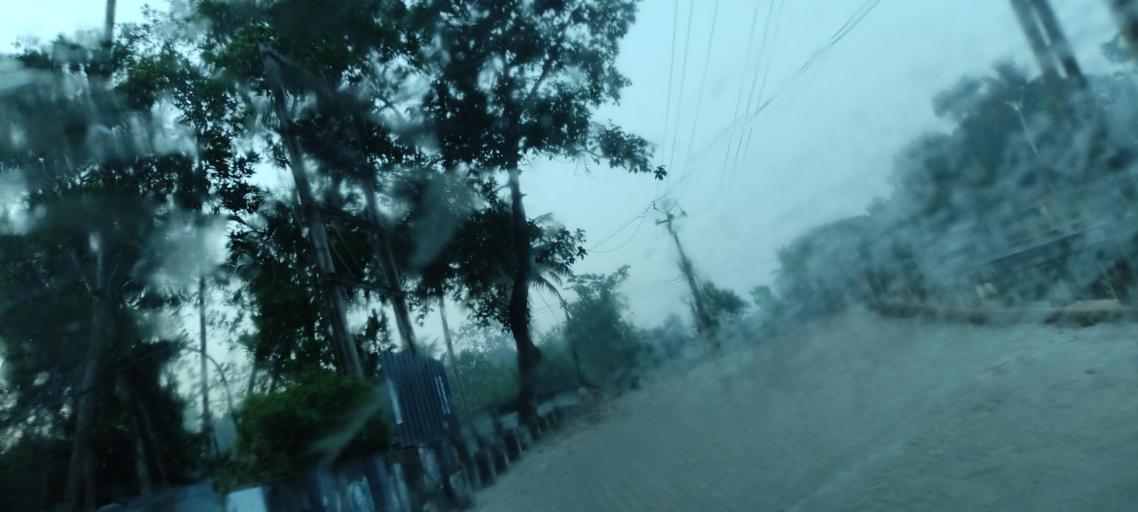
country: IN
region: Kerala
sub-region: Alappuzha
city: Alleppey
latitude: 9.5257
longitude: 76.3293
